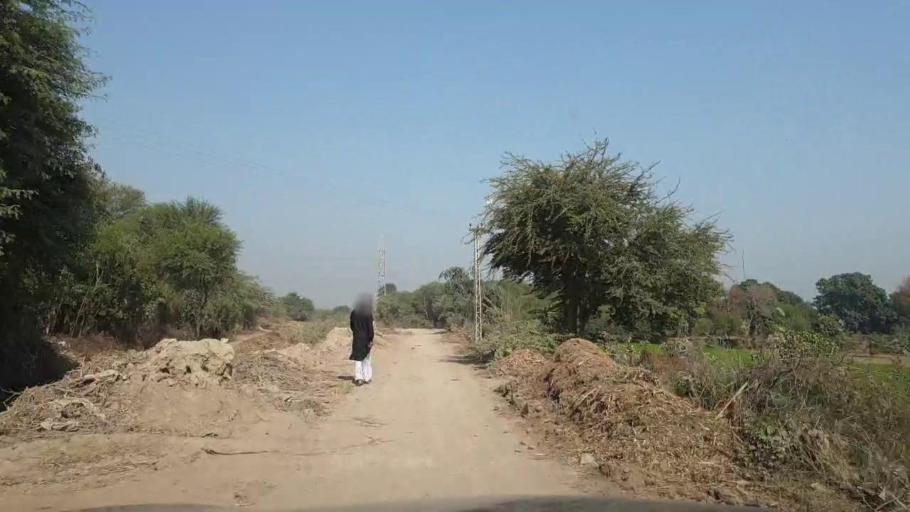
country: PK
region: Sindh
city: Tando Allahyar
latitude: 25.4692
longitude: 68.6925
